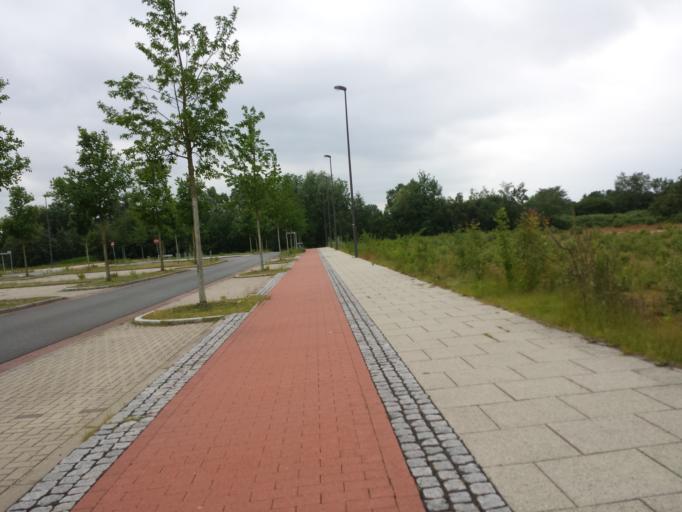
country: DE
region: Bremen
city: Bremen
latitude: 53.1029
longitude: 8.8482
